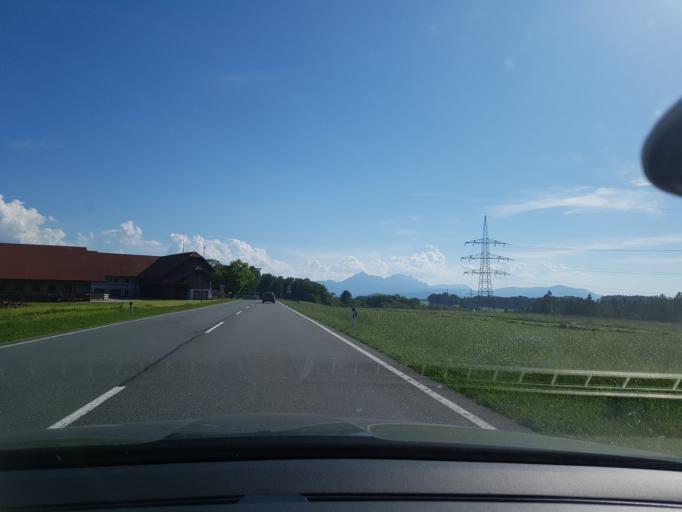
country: AT
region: Salzburg
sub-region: Politischer Bezirk Salzburg-Umgebung
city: Elixhausen
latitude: 47.8854
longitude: 13.0675
